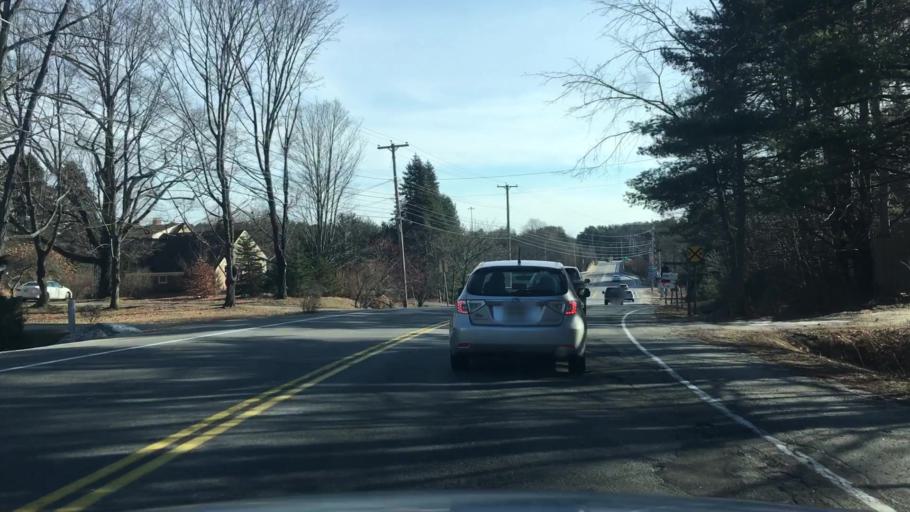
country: US
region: Maine
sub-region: Cumberland County
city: Falmouth
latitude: 43.7291
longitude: -70.2400
